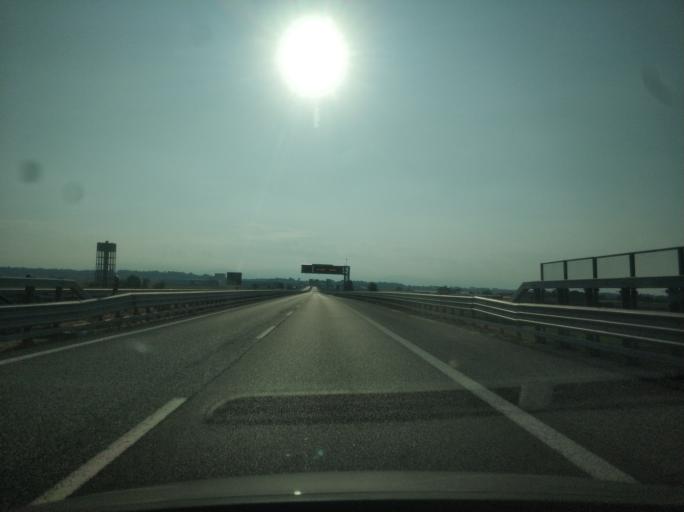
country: IT
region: Piedmont
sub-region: Provincia di Cuneo
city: Roreto
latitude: 44.6649
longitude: 7.8025
